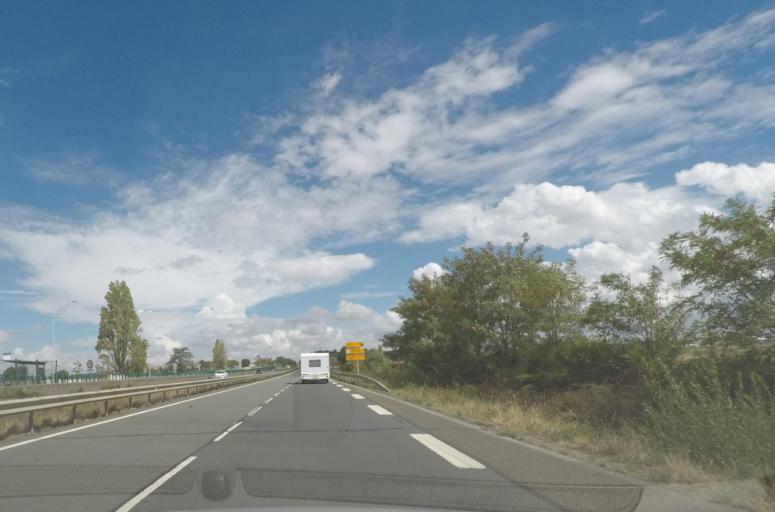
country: FR
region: Pays de la Loire
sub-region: Departement de la Sarthe
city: Arnage
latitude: 47.9504
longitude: 0.1956
